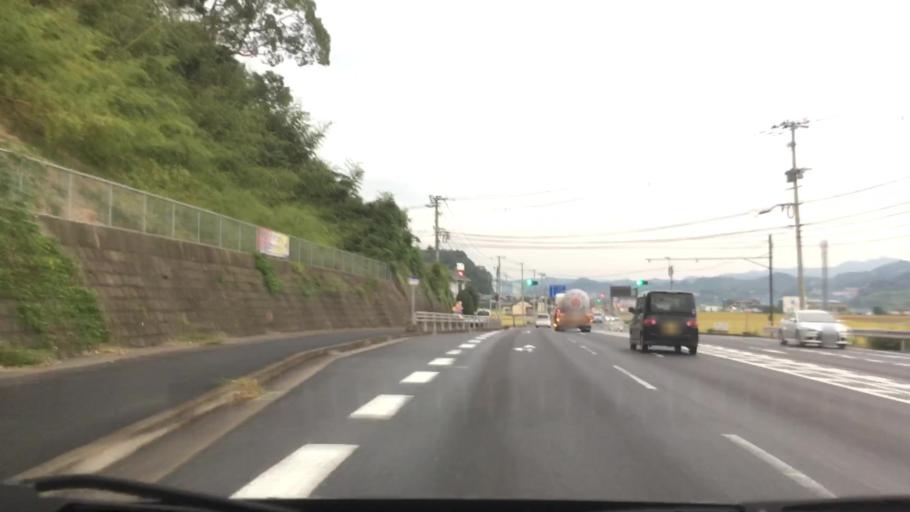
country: JP
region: Nagasaki
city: Sasebo
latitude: 33.1056
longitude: 129.7794
